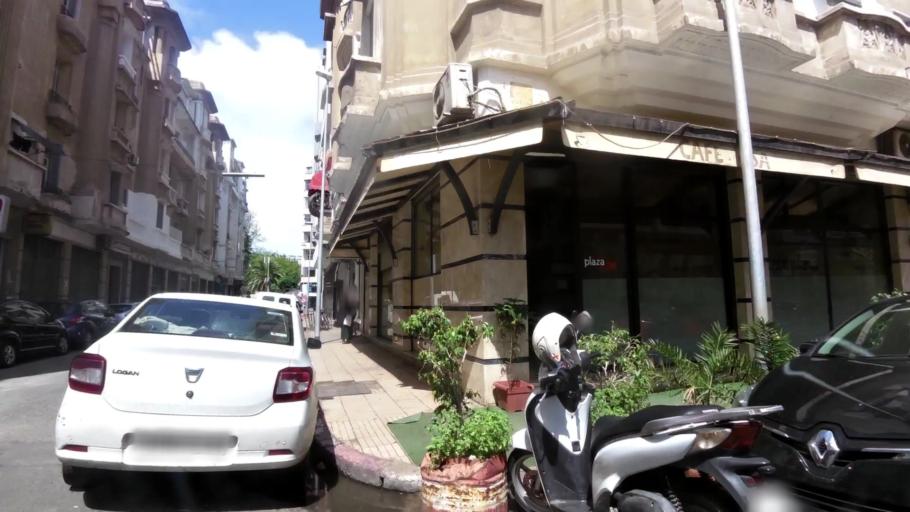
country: MA
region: Grand Casablanca
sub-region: Casablanca
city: Casablanca
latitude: 33.5942
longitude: -7.6201
